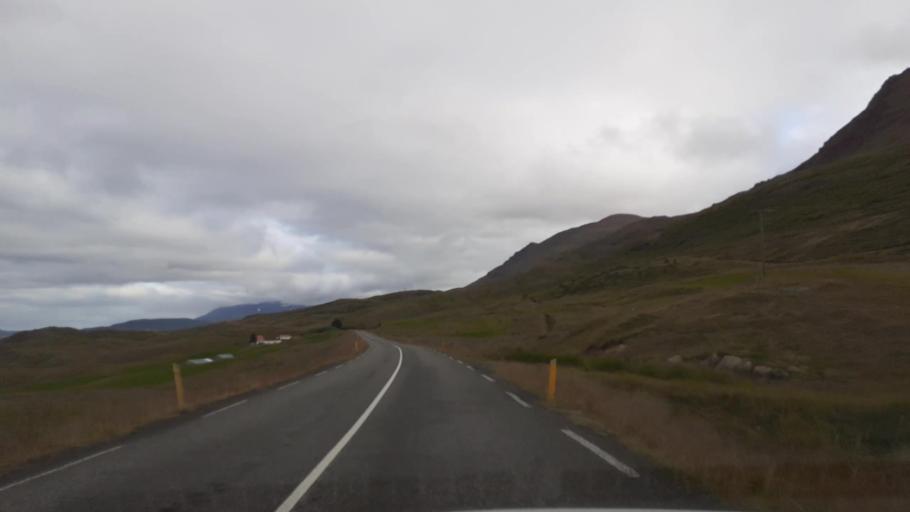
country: IS
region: Northeast
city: Akureyri
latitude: 65.8163
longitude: -18.0483
